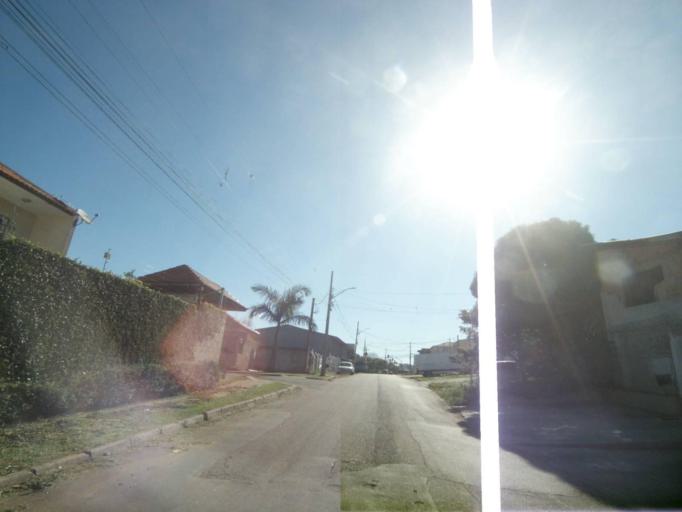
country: BR
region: Parana
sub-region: Curitiba
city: Curitiba
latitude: -25.4635
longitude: -49.3442
